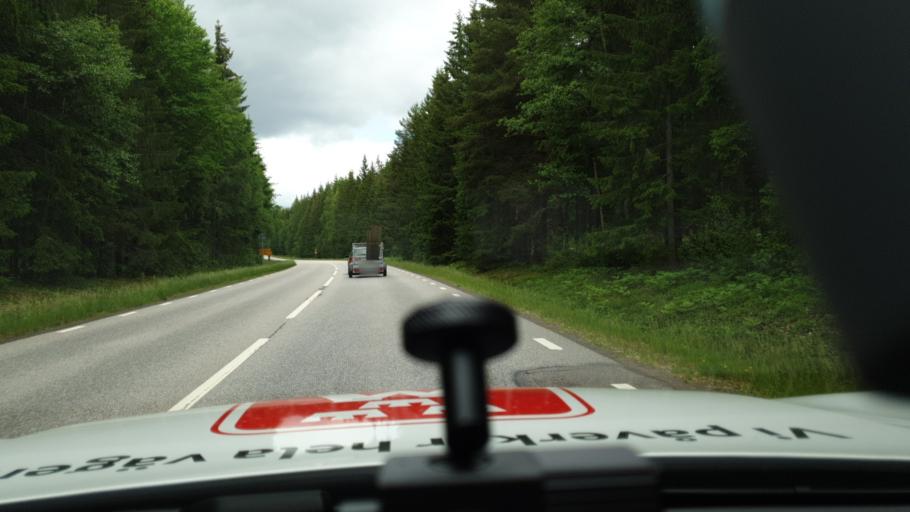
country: SE
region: Vaestra Goetaland
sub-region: Karlsborgs Kommun
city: Molltorp
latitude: 58.6405
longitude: 14.3965
